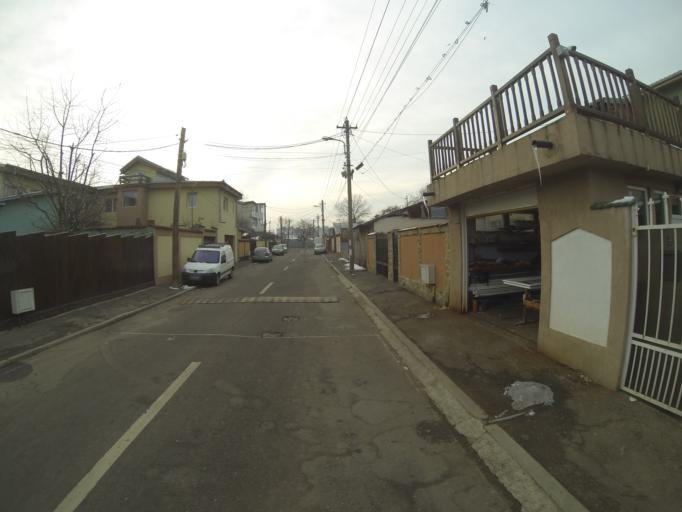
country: RO
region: Bucuresti
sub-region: Municipiul Bucuresti
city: Bucuresti
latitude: 44.3981
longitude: 26.0796
